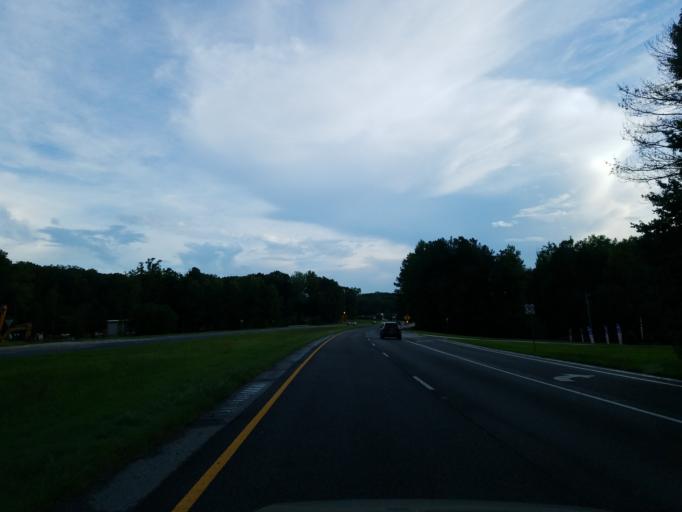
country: US
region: Georgia
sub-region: Forsyth County
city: Cumming
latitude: 34.2754
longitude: -84.0774
